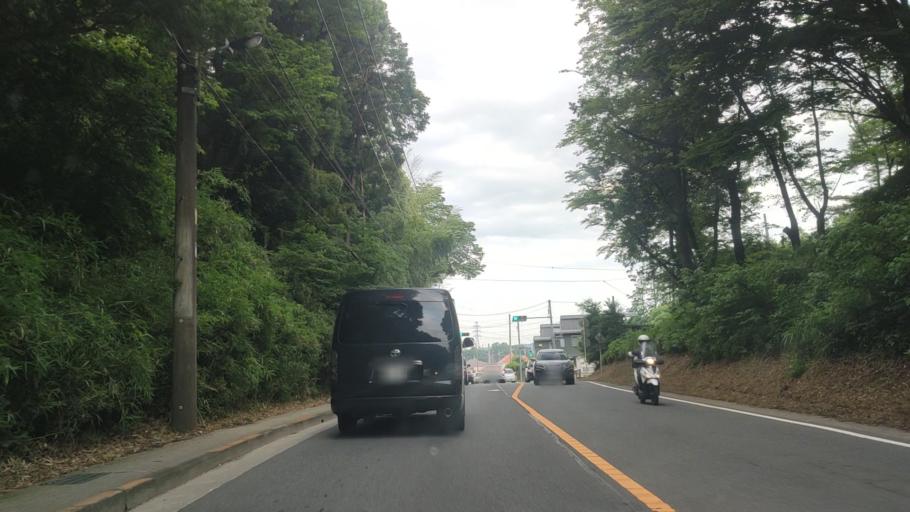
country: JP
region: Saitama
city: Hanno
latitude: 35.8112
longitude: 139.3003
